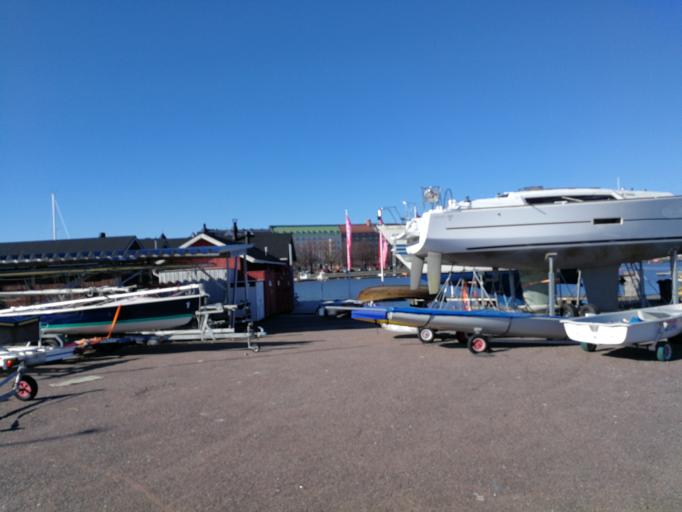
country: FI
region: Uusimaa
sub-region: Helsinki
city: Helsinki
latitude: 60.1526
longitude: 24.9466
